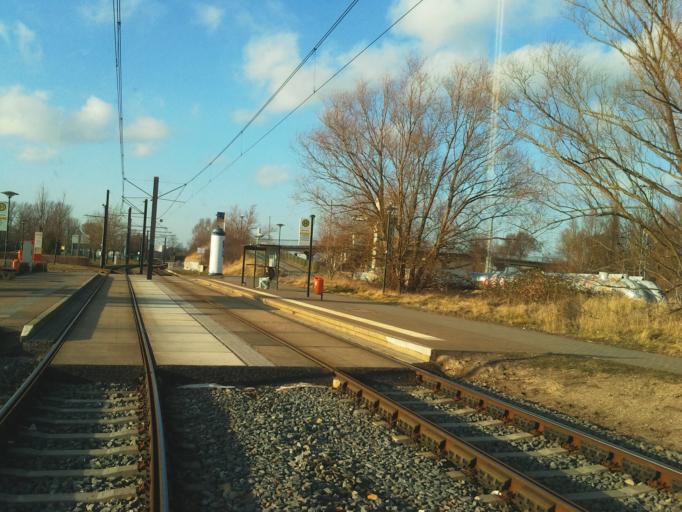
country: DE
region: Mecklenburg-Vorpommern
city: Rostock
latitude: 54.1104
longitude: 12.0809
